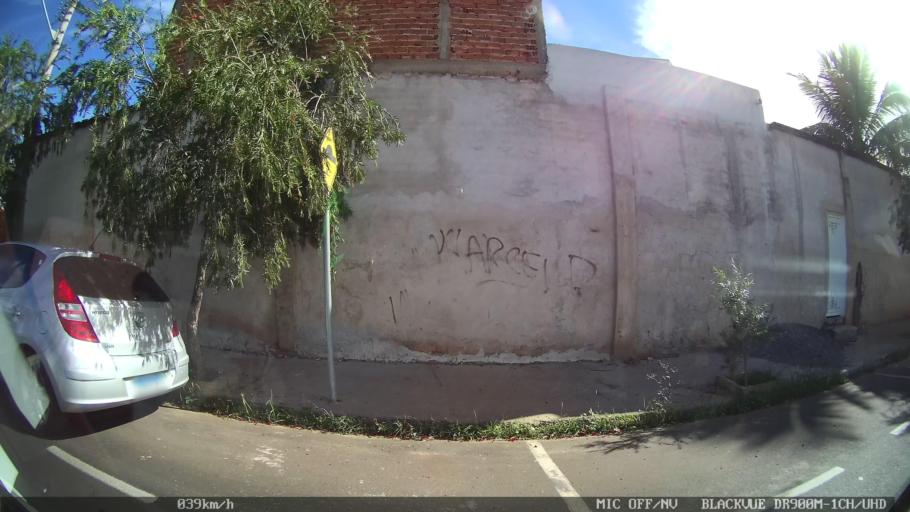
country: BR
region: Sao Paulo
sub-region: Catanduva
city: Catanduva
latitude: -21.1293
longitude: -48.9640
